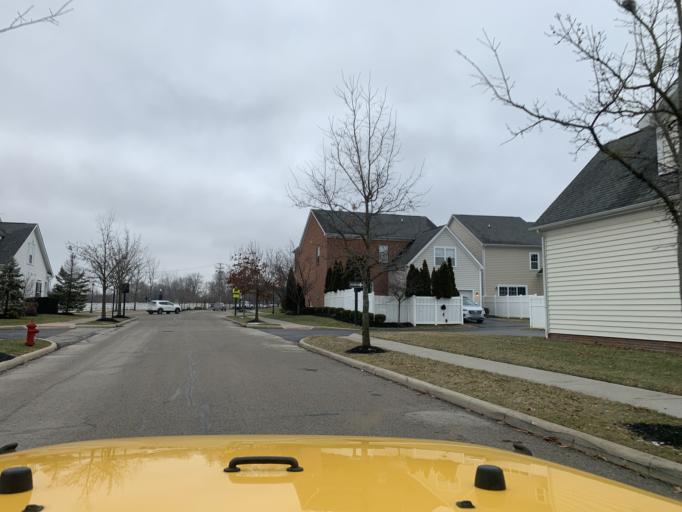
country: US
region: Ohio
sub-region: Franklin County
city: New Albany
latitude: 40.0870
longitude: -82.8036
